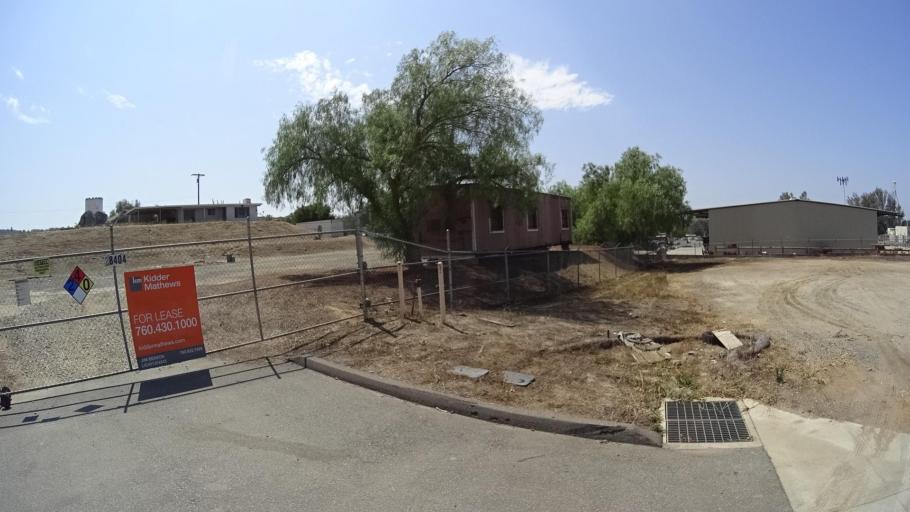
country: US
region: California
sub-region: San Diego County
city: Valley Center
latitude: 33.2297
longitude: -117.0220
